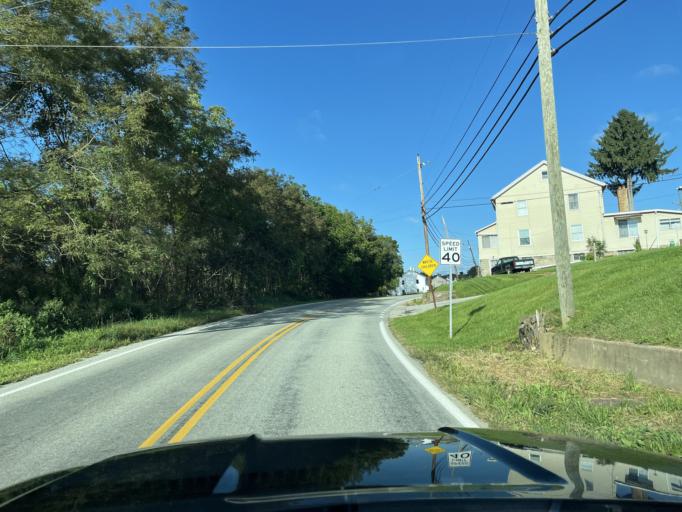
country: US
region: Pennsylvania
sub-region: Fayette County
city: South Uniontown
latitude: 39.8784
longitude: -79.7689
